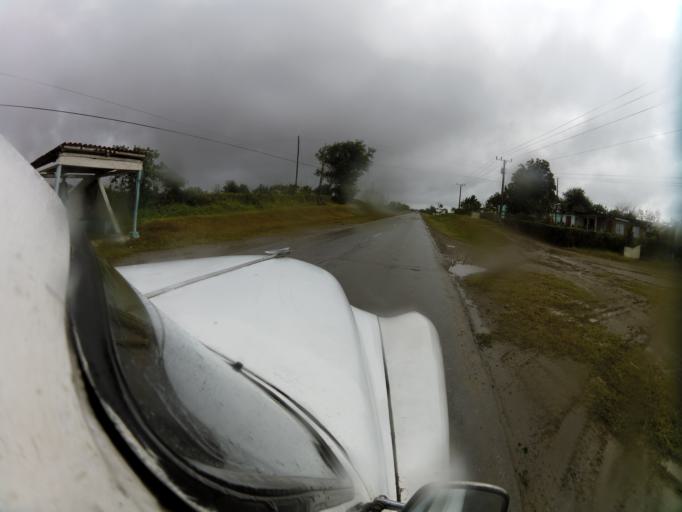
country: CU
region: Las Tunas
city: Las Tunas
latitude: 20.9199
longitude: -76.8501
